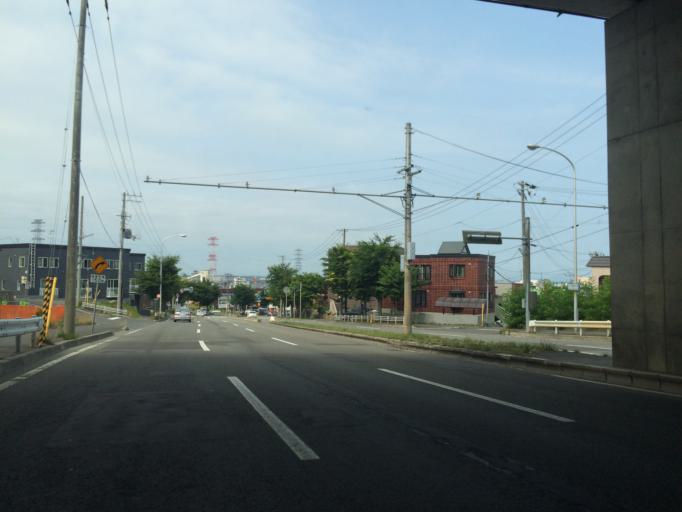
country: JP
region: Hokkaido
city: Sapporo
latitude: 43.0920
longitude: 141.2601
